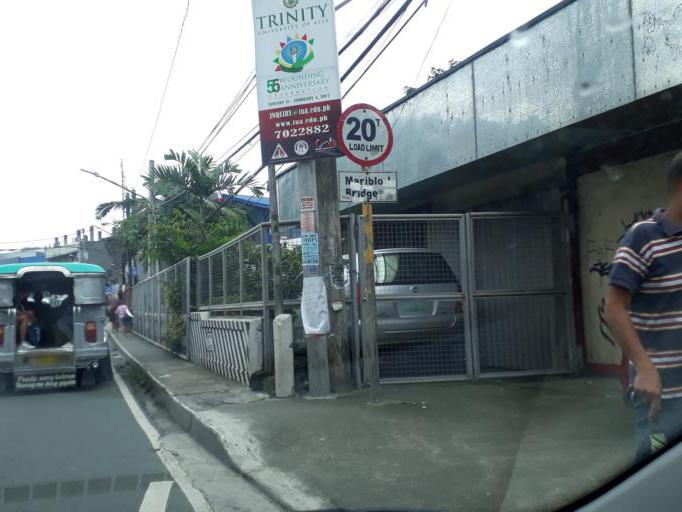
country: PH
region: Calabarzon
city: Del Monte
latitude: 14.6358
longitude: 121.0181
